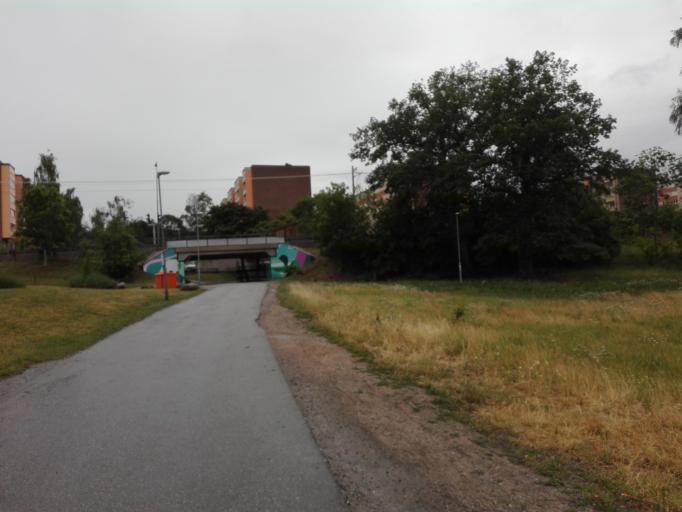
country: SE
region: Stockholm
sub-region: Nacka Kommun
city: Fisksatra
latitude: 59.2945
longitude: 18.2534
